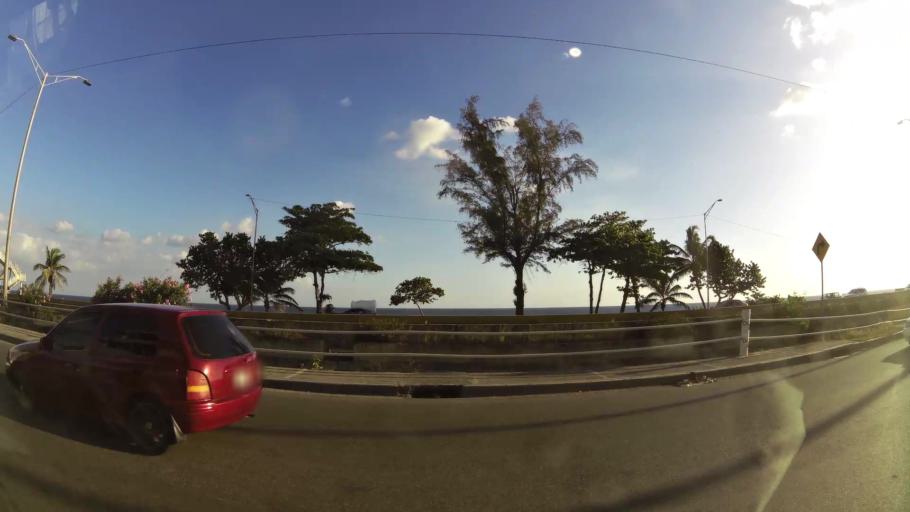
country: DO
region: Santo Domingo
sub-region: Santo Domingo
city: Santo Domingo Este
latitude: 18.4653
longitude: -69.8159
